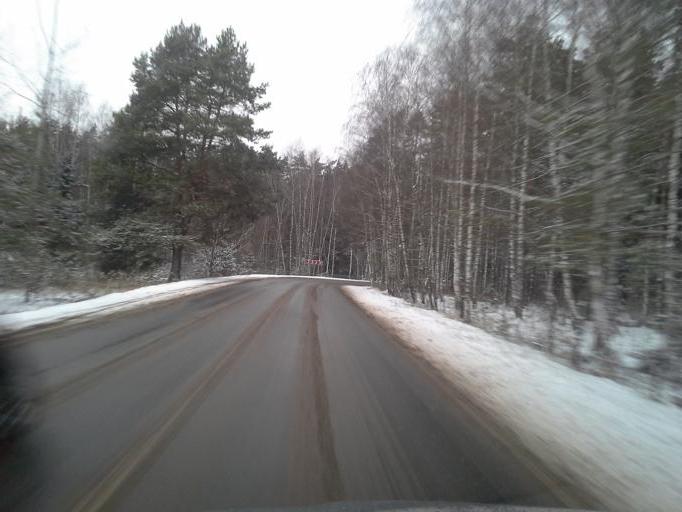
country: RU
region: Moskovskaya
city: Nikolina Gora
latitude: 55.7434
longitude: 37.0753
